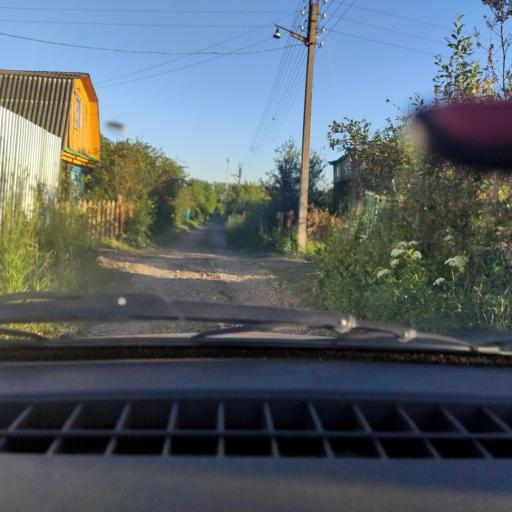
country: RU
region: Bashkortostan
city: Karmaskaly
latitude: 54.3670
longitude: 55.9031
